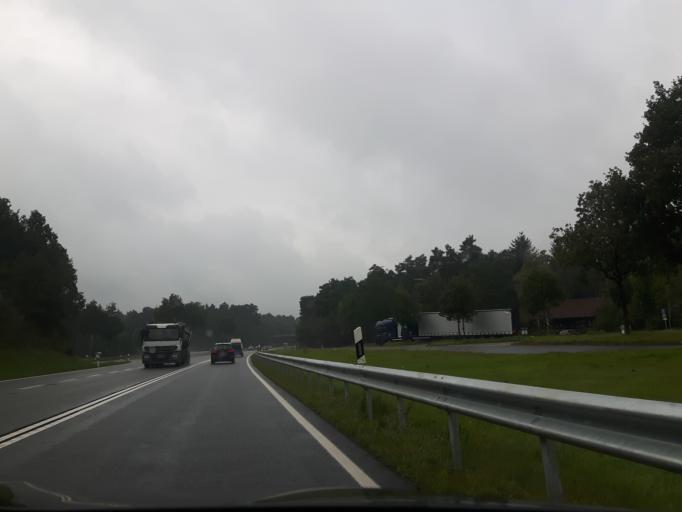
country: DE
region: Lower Saxony
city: Lingen
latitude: 52.5018
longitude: 7.3404
